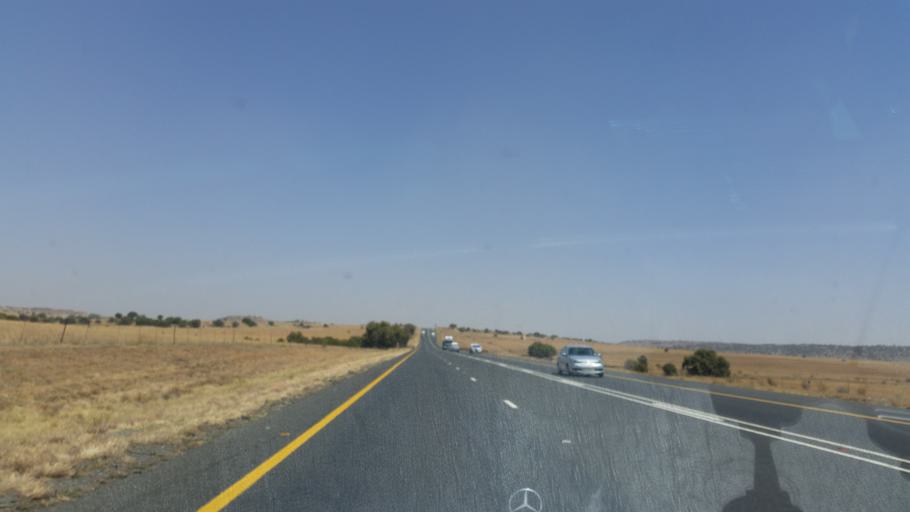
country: ZA
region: Orange Free State
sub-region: Lejweleputswa District Municipality
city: Winburg
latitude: -28.6851
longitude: 26.8231
